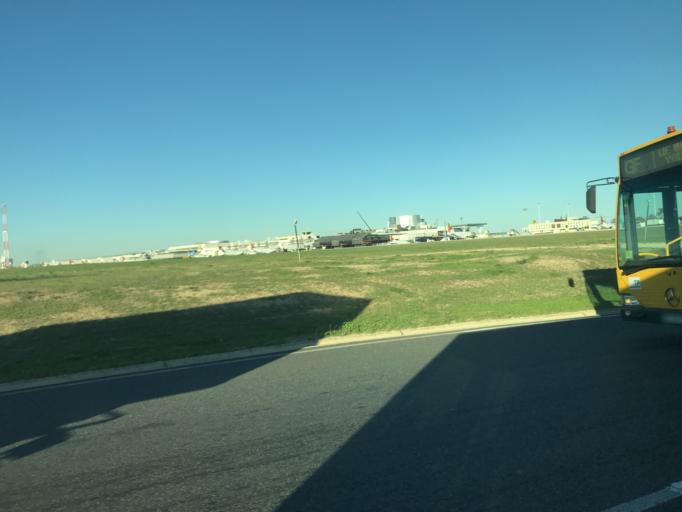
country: PT
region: Lisbon
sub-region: Loures
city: Moscavide
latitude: 38.7652
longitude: -9.1332
